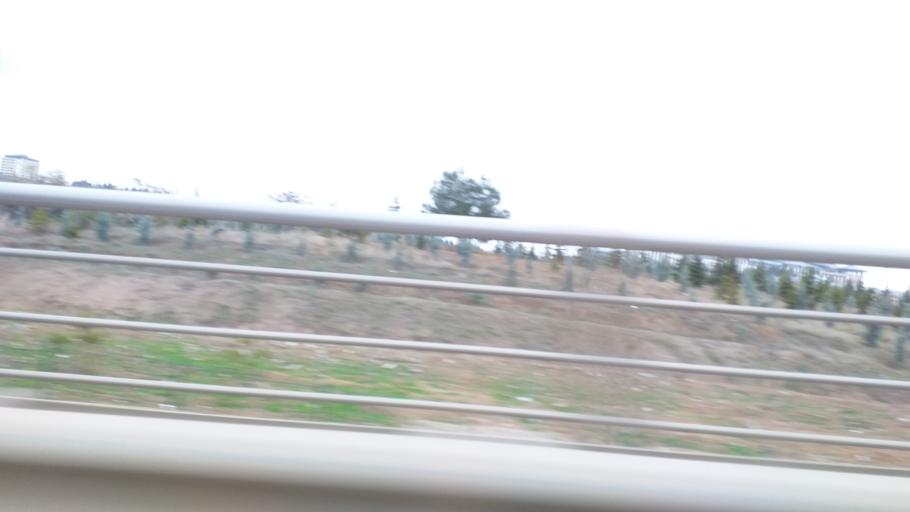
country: TR
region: Ankara
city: Ankara
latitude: 39.9223
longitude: 32.7977
